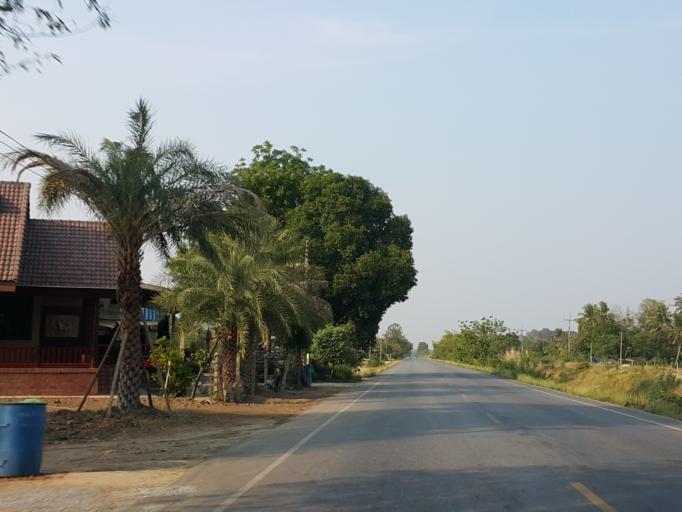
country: TH
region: Chai Nat
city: Sankhaburi
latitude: 14.9989
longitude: 100.1211
